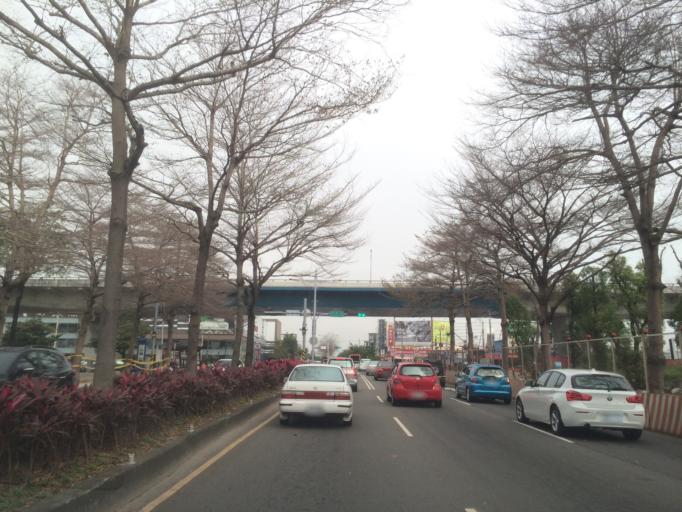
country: TW
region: Taiwan
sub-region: Taichung City
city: Taichung
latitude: 24.2001
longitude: 120.6867
